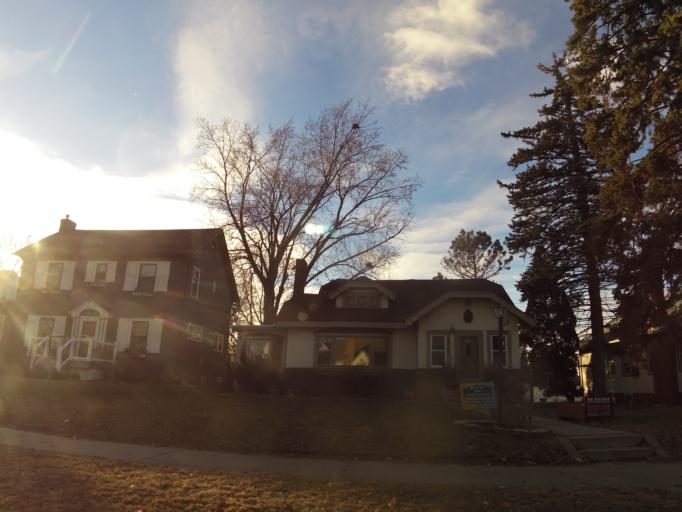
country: US
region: Minnesota
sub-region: Hennepin County
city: Richfield
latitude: 44.9173
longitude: -93.2729
